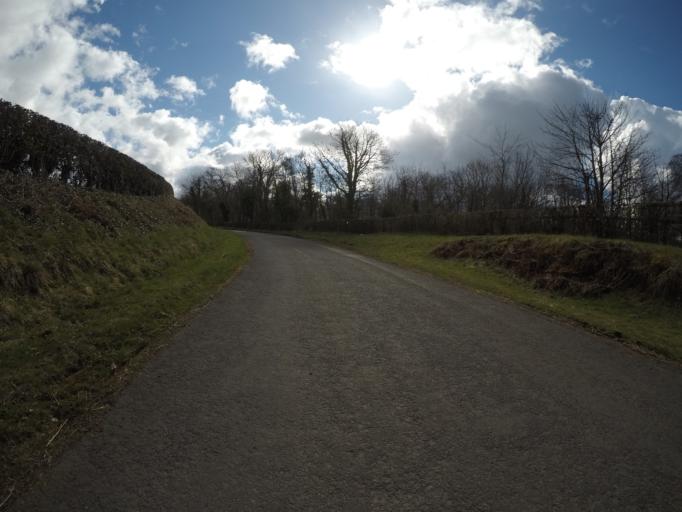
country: GB
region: Scotland
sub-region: North Ayrshire
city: Beith
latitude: 55.7371
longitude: -4.6603
